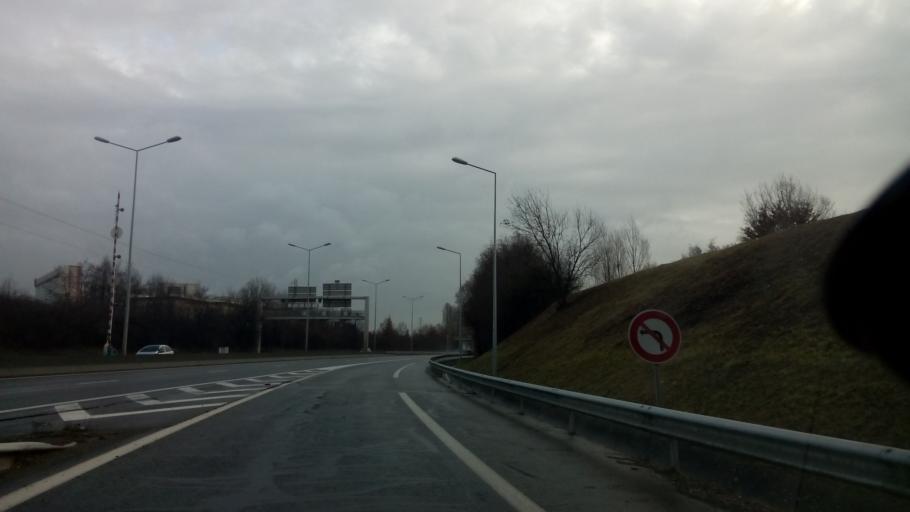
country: FR
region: Rhone-Alpes
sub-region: Departement du Rhone
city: Venissieux
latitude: 45.6863
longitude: 4.8634
